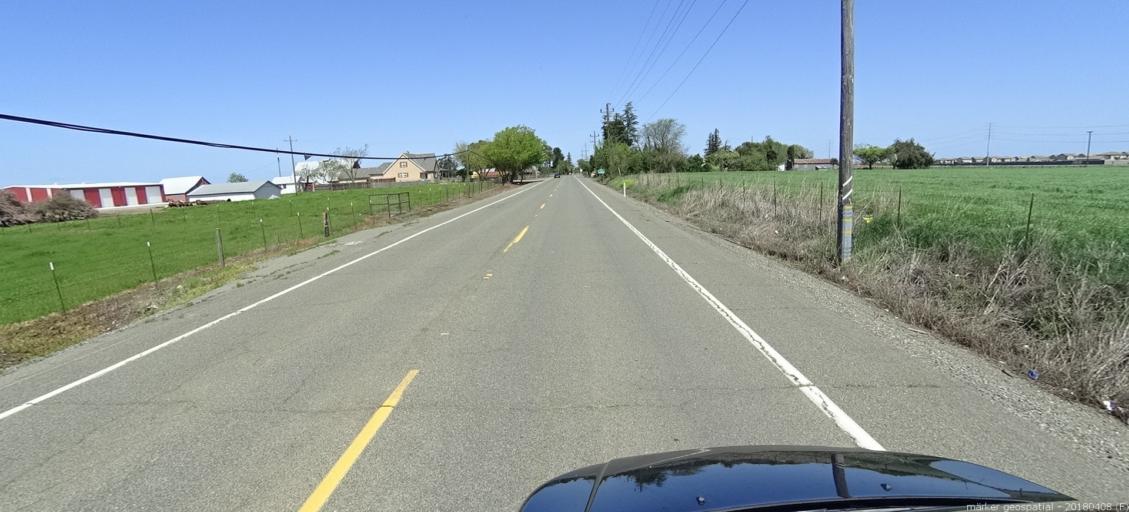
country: US
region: California
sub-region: Sacramento County
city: Laguna
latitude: 38.3693
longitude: -121.4543
